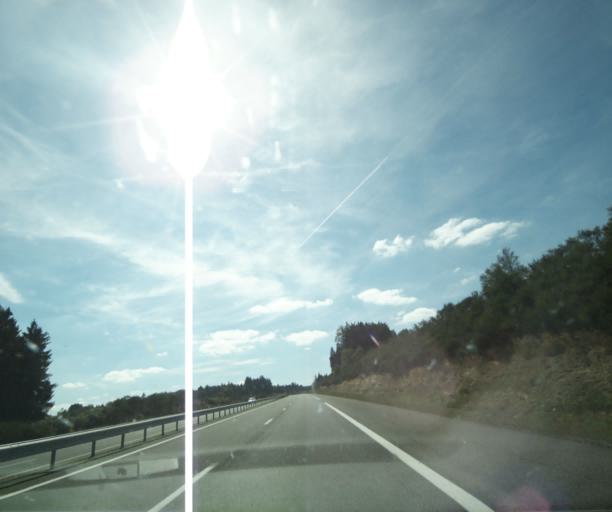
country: FR
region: Auvergne
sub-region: Departement du Puy-de-Dome
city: Gelles
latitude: 45.7443
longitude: 2.7124
